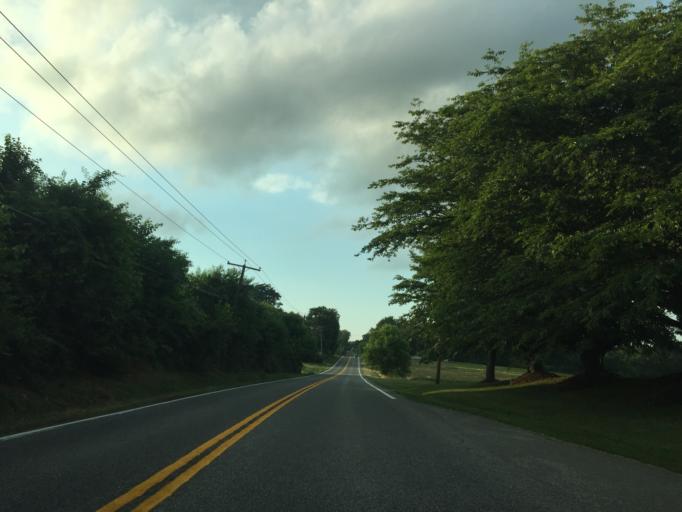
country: US
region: Maryland
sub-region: Harford County
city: Jarrettsville
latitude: 39.5712
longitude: -76.4996
